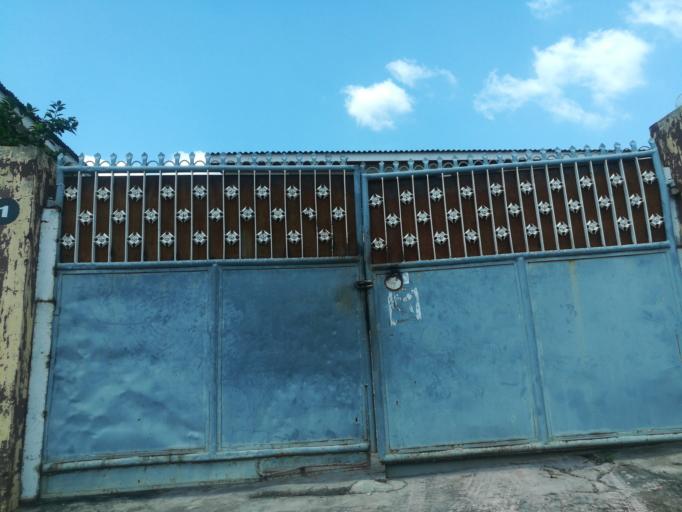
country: NG
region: Oyo
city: Ibadan
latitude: 7.3558
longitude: 3.8669
